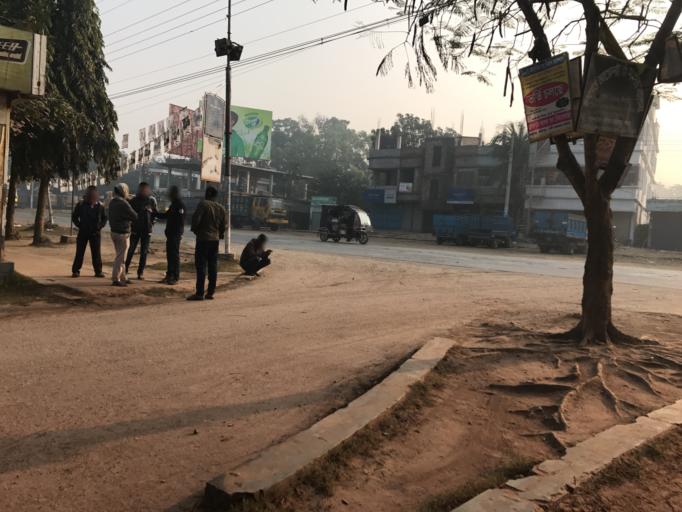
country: BD
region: Khulna
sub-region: Magura
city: Magura
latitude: 23.4966
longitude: 89.4328
